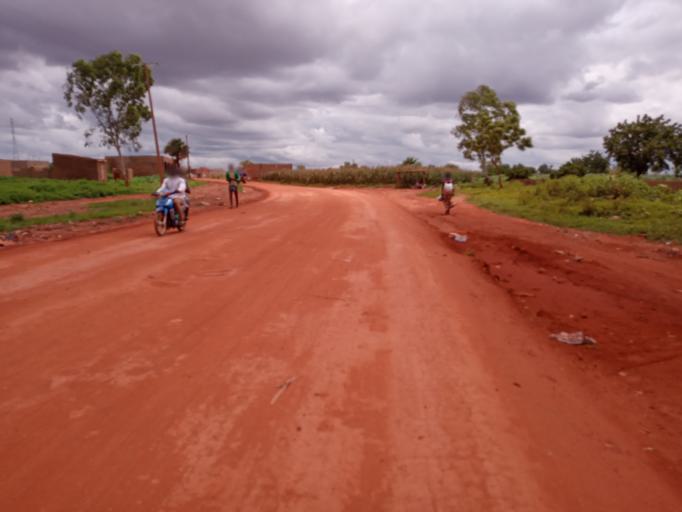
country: ML
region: Bamako
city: Bamako
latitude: 12.5444
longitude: -7.9941
